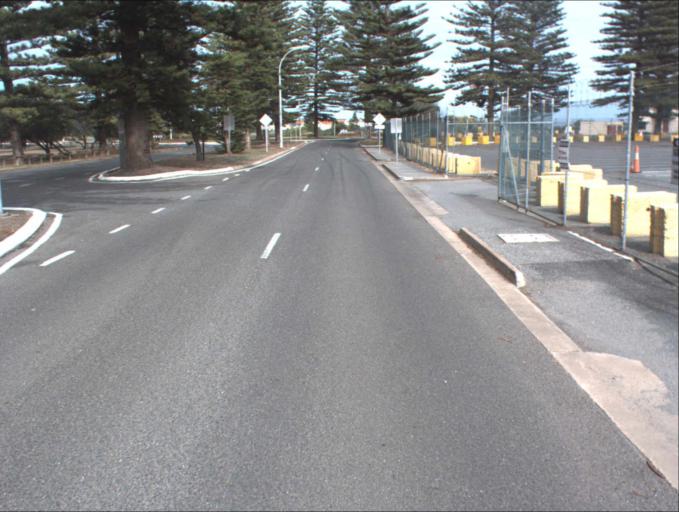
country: AU
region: South Australia
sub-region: Port Adelaide Enfield
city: Birkenhead
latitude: -34.7790
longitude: 138.4833
